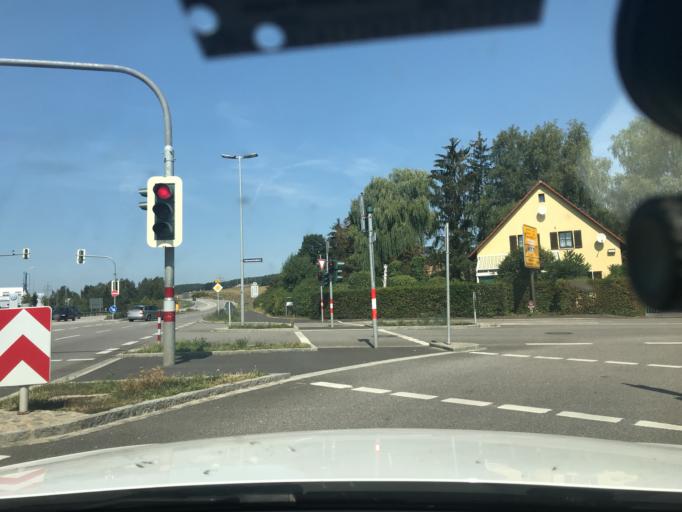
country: DE
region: Bavaria
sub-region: Upper Palatinate
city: Amberg
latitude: 49.4493
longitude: 11.8290
